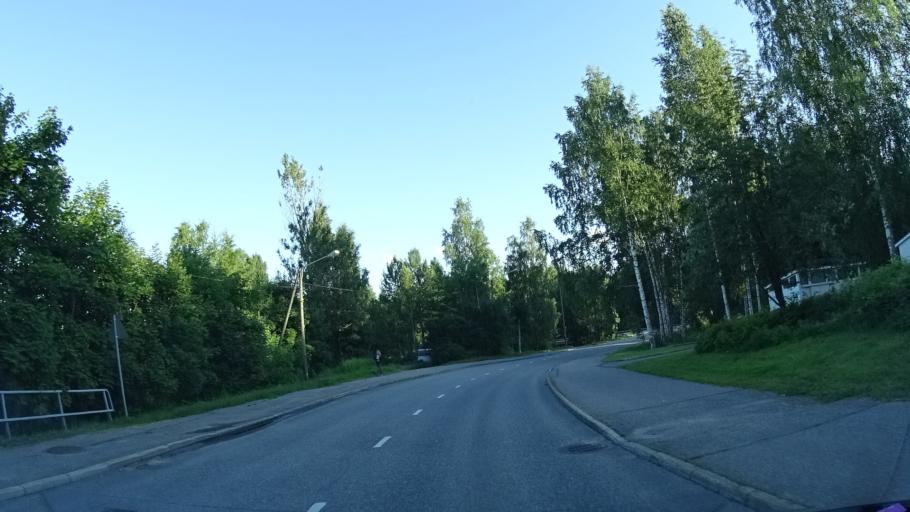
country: FI
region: Uusimaa
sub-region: Helsinki
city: Teekkarikylae
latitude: 60.2748
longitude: 24.8749
